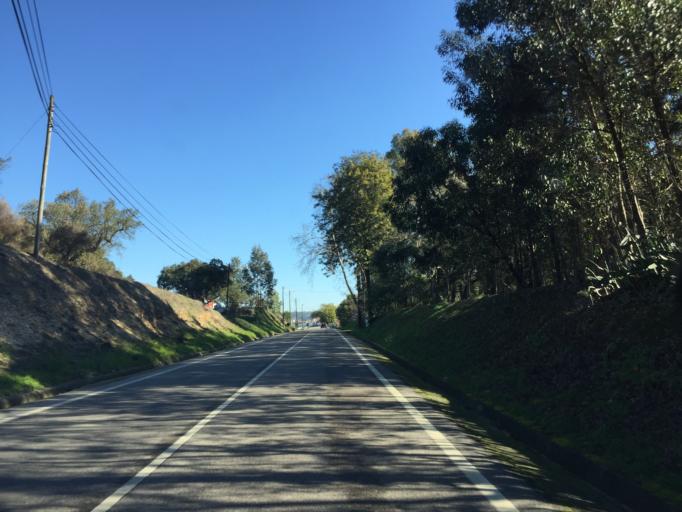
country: PT
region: Portalegre
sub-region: Ponte de Sor
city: Ponte de Sor
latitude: 39.3291
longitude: -7.9936
